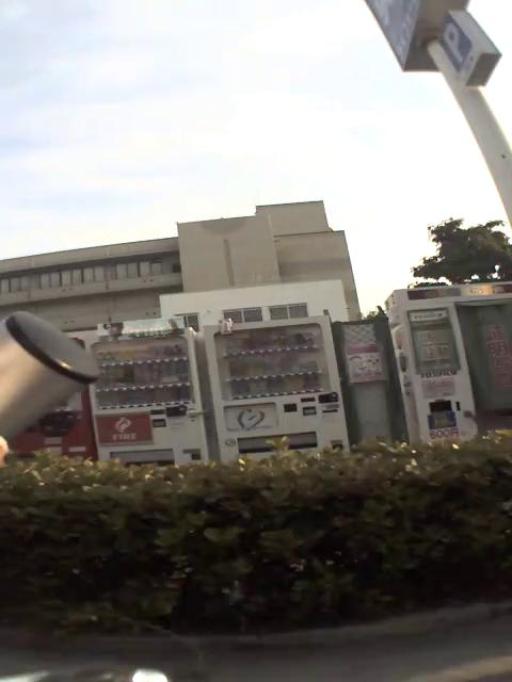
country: JP
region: Osaka
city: Kadoma
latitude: 34.7340
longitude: 135.5739
